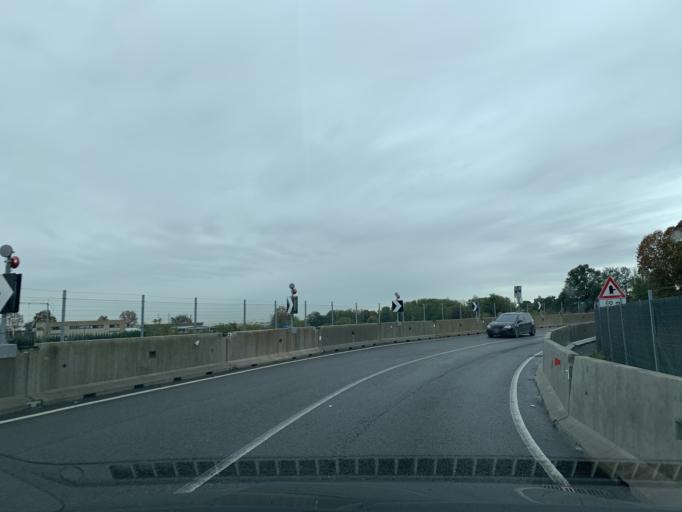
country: IT
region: Lombardy
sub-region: Provincia di Como
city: Bregnano
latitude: 45.6971
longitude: 9.0684
